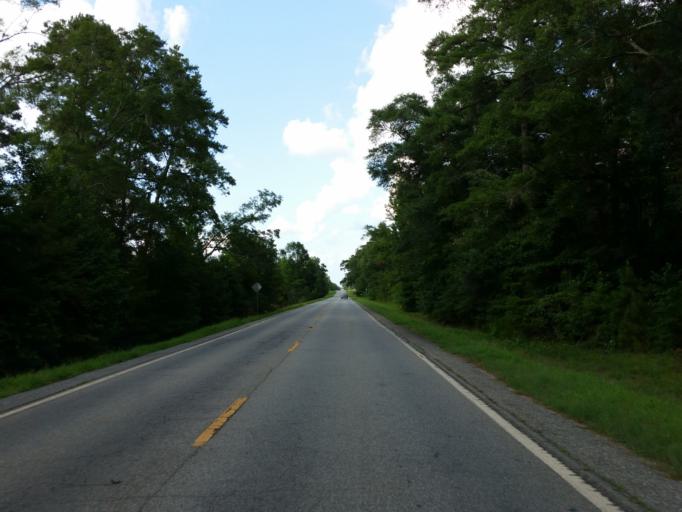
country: US
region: Georgia
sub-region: Lee County
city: Leesburg
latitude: 31.7812
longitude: -84.1357
